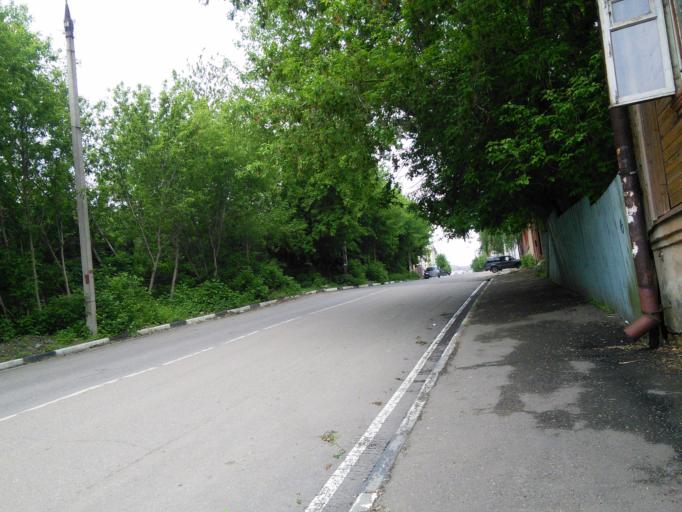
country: RU
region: Moskovskaya
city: Serpukhov
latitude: 54.9117
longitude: 37.4126
